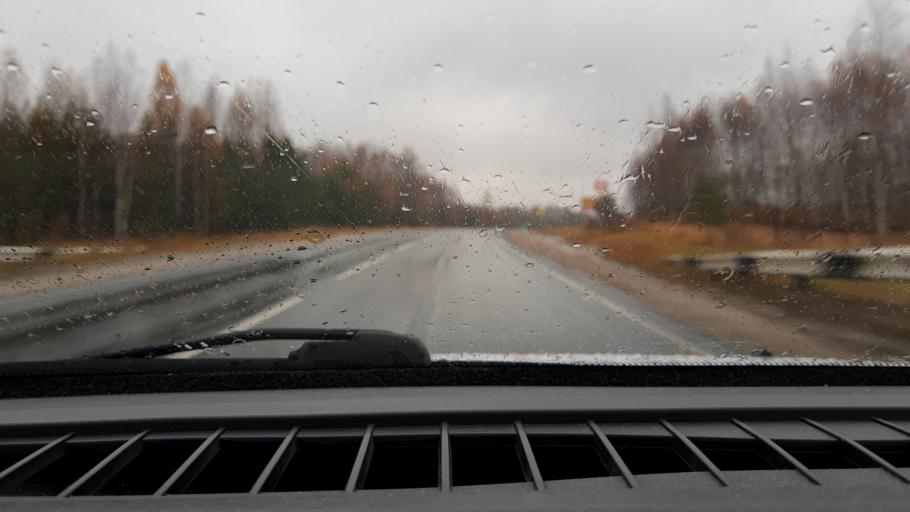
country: RU
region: Nizjnij Novgorod
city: Sitniki
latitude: 56.4810
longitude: 44.0231
